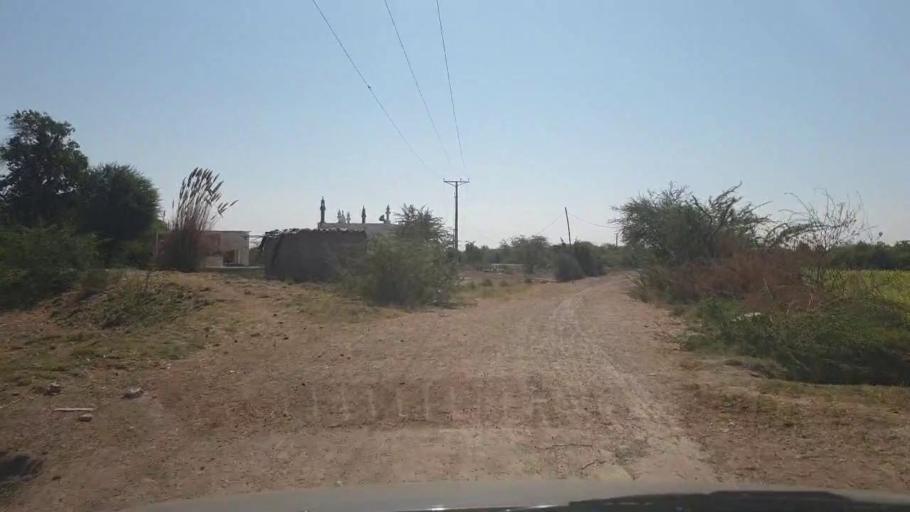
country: PK
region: Sindh
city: Umarkot
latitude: 25.3854
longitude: 69.6208
